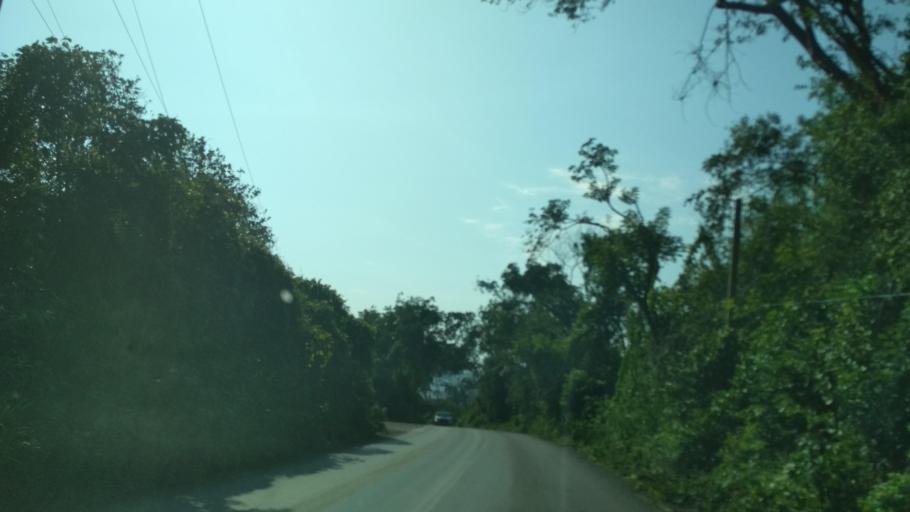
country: MX
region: Veracruz
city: Agua Dulce
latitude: 20.4020
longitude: -97.2245
